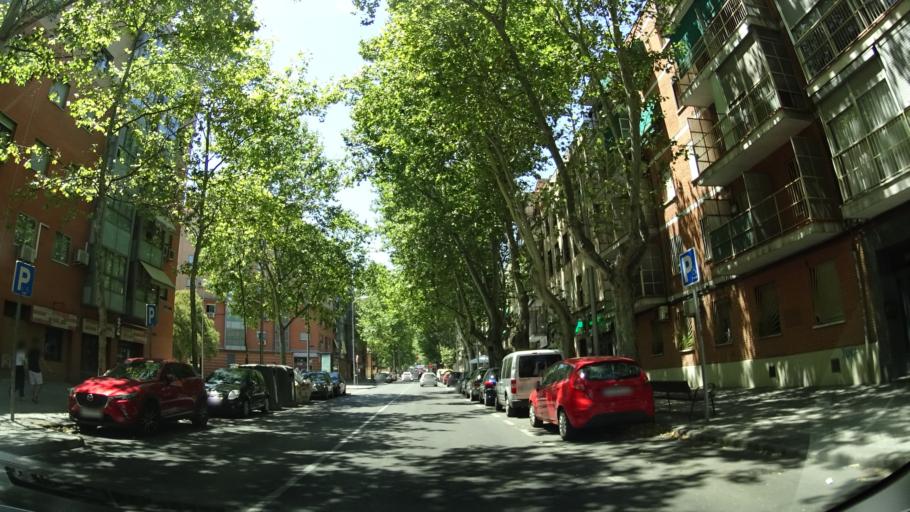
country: ES
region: Madrid
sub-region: Provincia de Madrid
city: Latina
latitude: 40.3799
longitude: -3.7462
